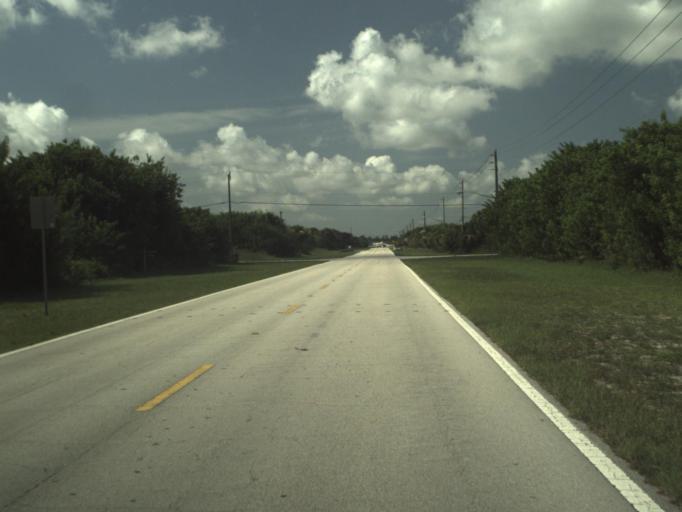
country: US
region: Florida
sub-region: Saint Lucie County
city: Port Saint Lucie
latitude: 27.2194
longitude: -80.3720
